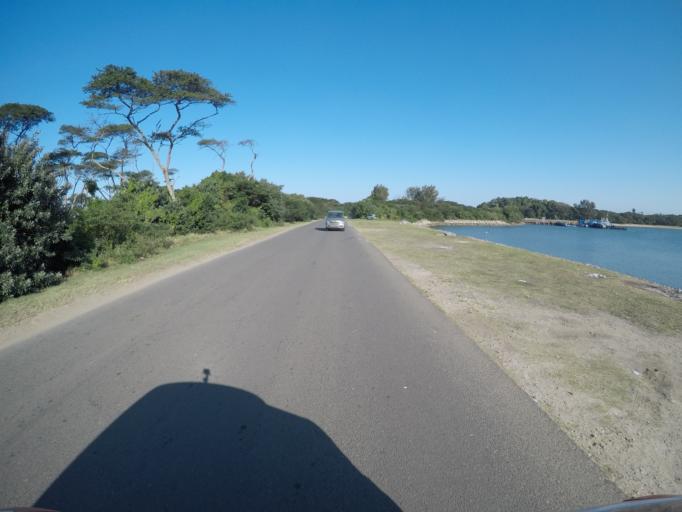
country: ZA
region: KwaZulu-Natal
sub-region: uThungulu District Municipality
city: Richards Bay
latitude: -28.7969
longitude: 32.0822
